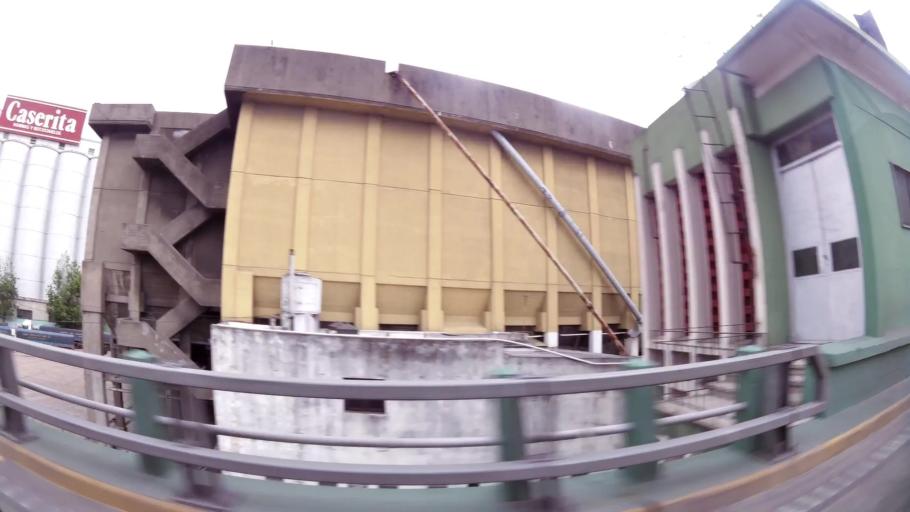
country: AR
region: Buenos Aires
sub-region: Partido de Avellaneda
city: Avellaneda
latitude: -34.6562
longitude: -58.3712
